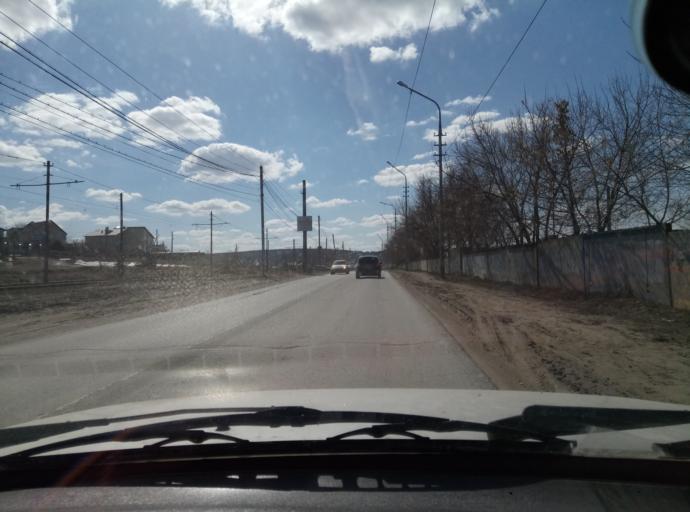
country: RU
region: Saratov
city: Sokolovyy
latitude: 51.5826
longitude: 45.9008
